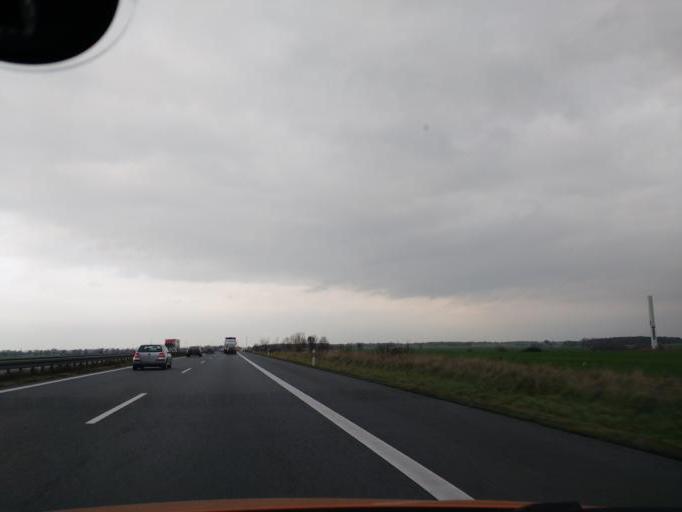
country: DE
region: Brandenburg
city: Fehrbellin
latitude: 52.8639
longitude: 12.7658
